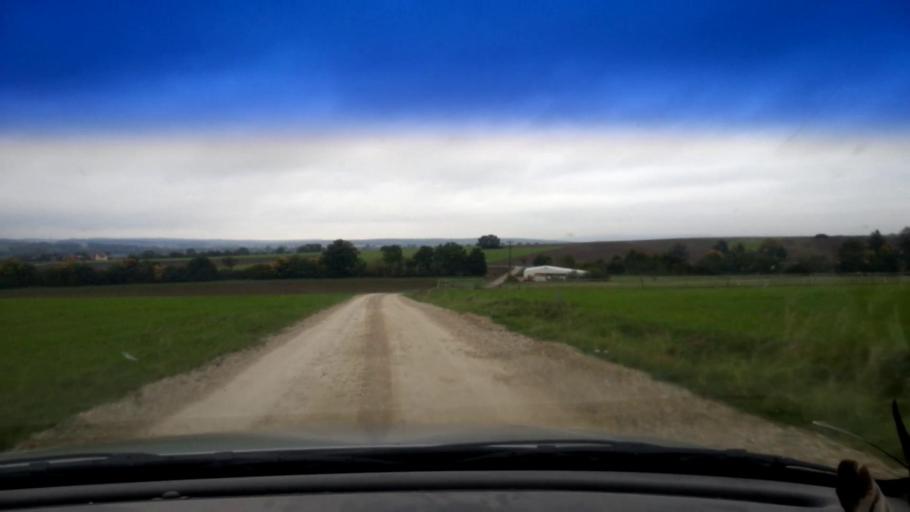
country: DE
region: Bavaria
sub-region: Upper Franconia
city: Litzendorf
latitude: 49.9365
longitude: 11.0046
